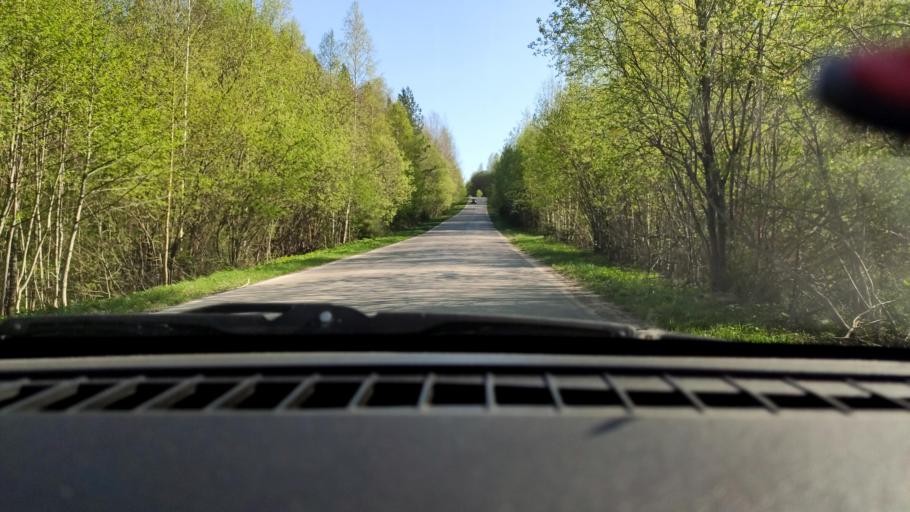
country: RU
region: Perm
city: Overyata
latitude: 58.0694
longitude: 56.0017
